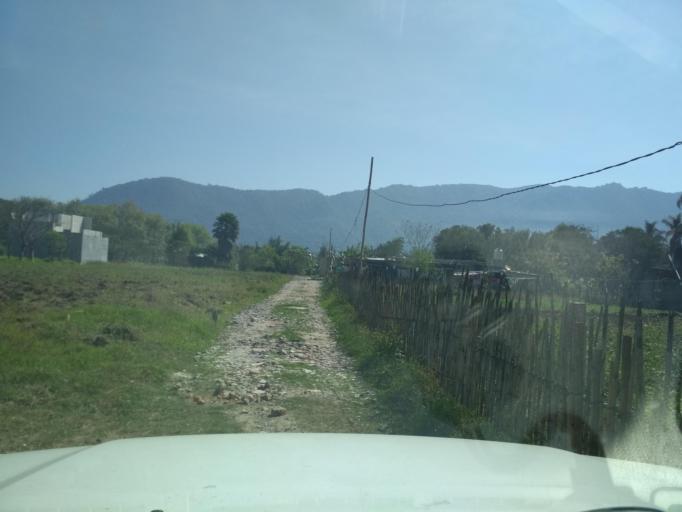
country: MX
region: Veracruz
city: Jalapilla
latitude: 18.8172
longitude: -97.0874
